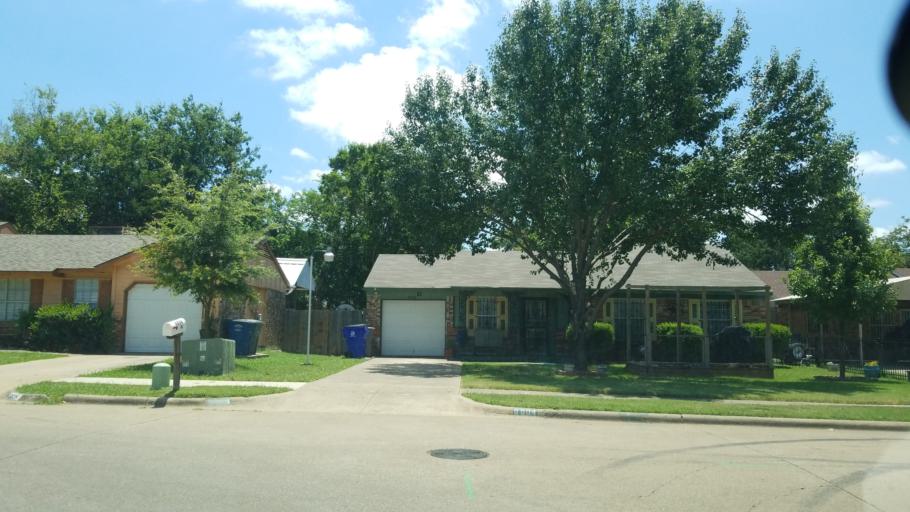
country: US
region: Texas
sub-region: Dallas County
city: Balch Springs
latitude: 32.7411
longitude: -96.7045
